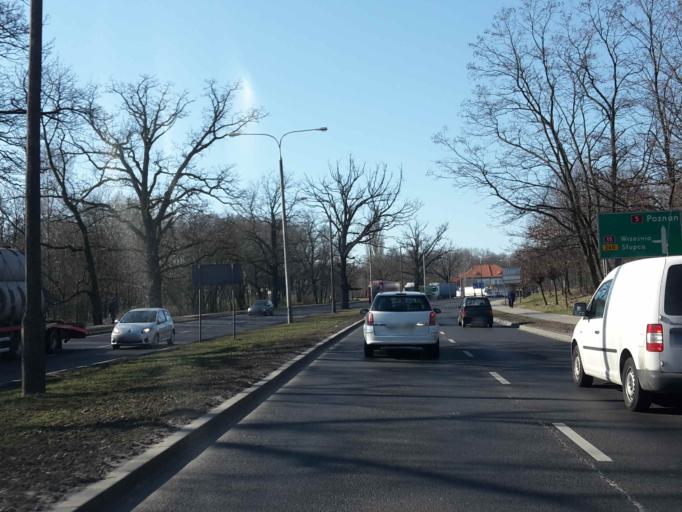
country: PL
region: Greater Poland Voivodeship
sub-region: Powiat gnieznienski
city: Gniezno
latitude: 52.5364
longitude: 17.5859
